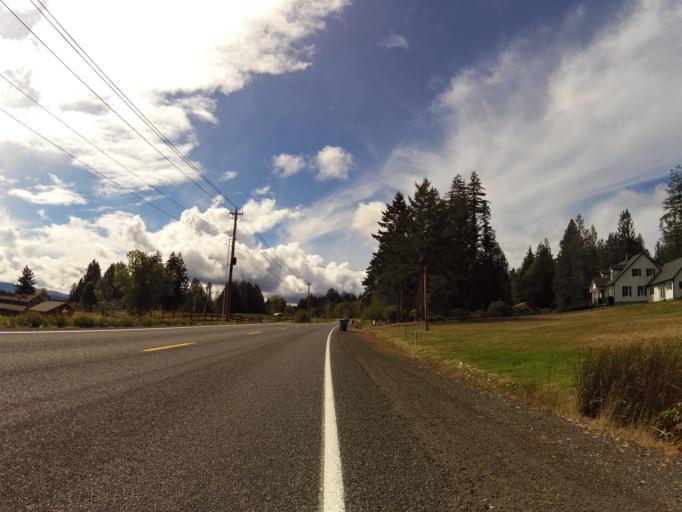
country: US
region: Washington
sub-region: Mason County
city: Shelton
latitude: 47.1540
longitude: -123.0566
